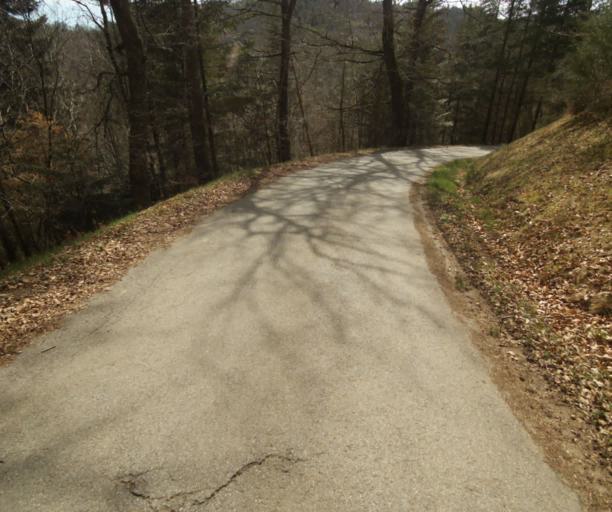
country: FR
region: Limousin
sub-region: Departement de la Correze
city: Naves
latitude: 45.3447
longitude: 1.8040
